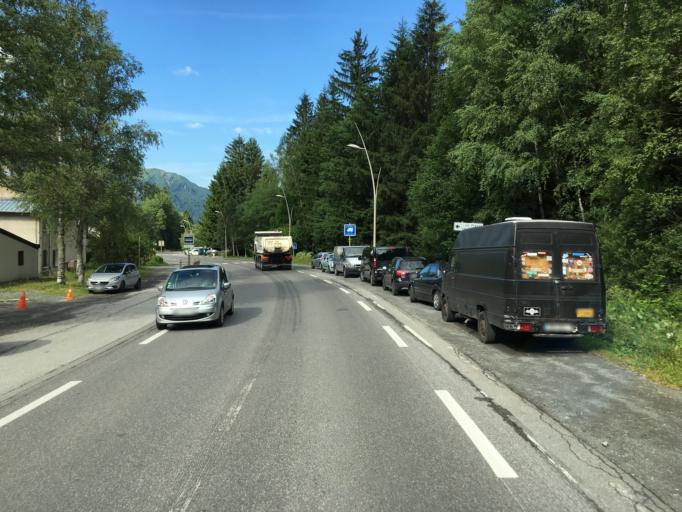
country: FR
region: Rhone-Alpes
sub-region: Departement de la Haute-Savoie
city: Chamonix-Mont-Blanc
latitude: 45.9303
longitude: 6.8804
